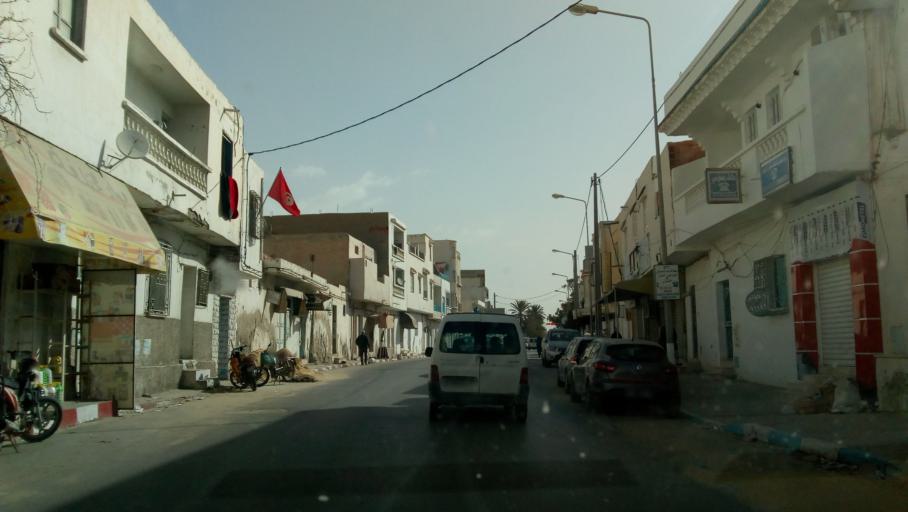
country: TN
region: Qabis
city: Gabes
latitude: 33.8848
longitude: 10.0892
